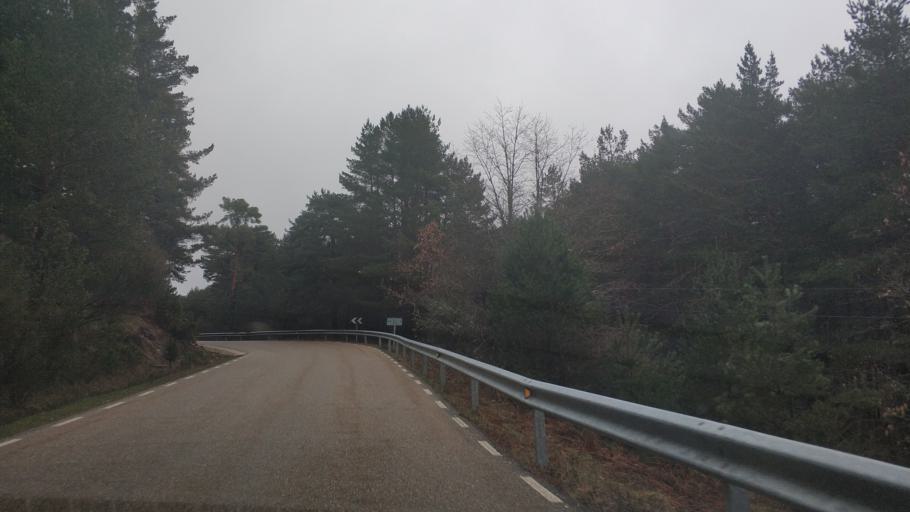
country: ES
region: Castille and Leon
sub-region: Provincia de Burgos
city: Quintanar de la Sierra
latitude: 42.0205
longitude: -3.0154
